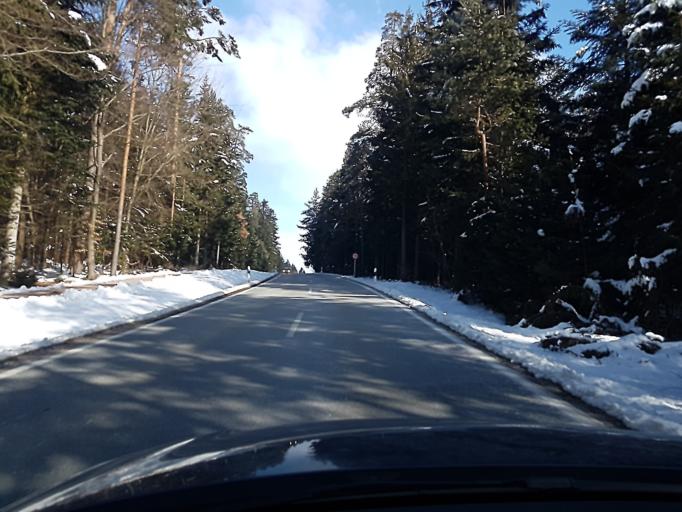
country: DE
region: Baden-Wuerttemberg
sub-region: Freiburg Region
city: Konigsfeld im Schwarzwald
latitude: 48.1621
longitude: 8.4556
